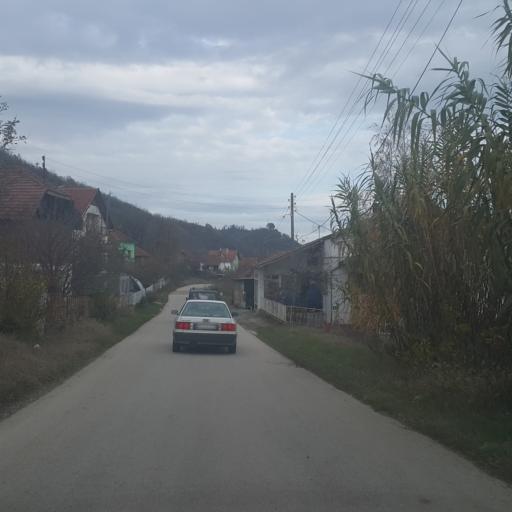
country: RS
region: Central Serbia
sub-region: Zajecarski Okrug
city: Knjazevac
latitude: 43.5902
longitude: 22.2522
